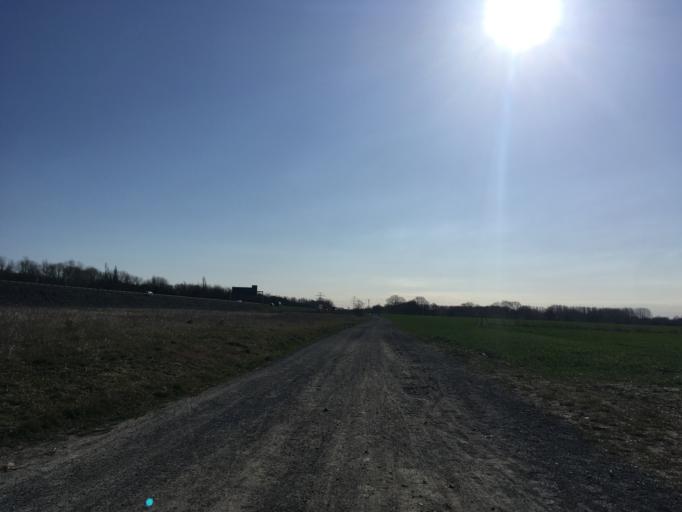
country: DE
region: Berlin
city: Buchholz
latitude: 52.6319
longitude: 13.4491
